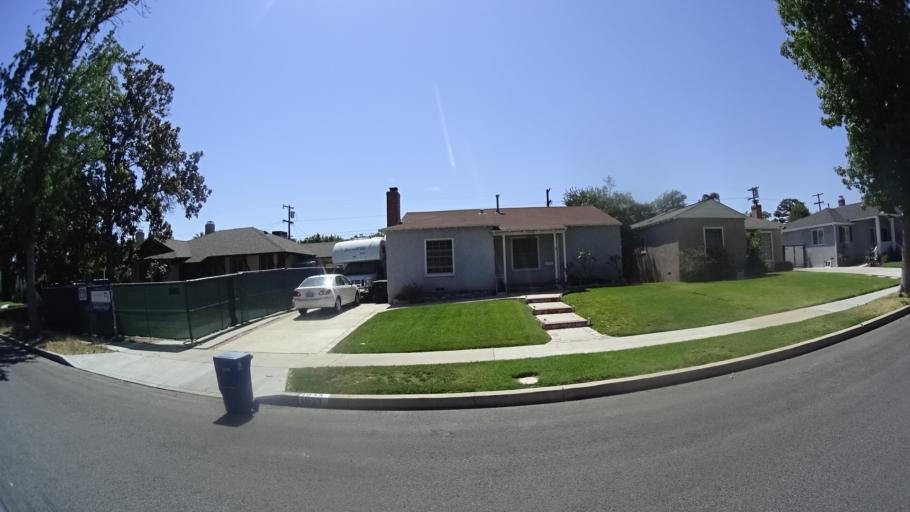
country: US
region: California
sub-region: Los Angeles County
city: North Hollywood
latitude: 34.1824
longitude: -118.3575
